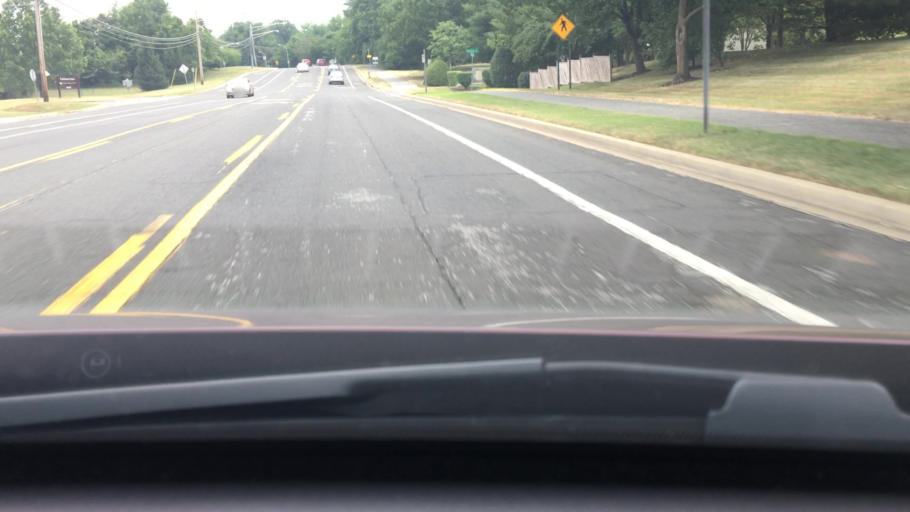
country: US
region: Maryland
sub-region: Montgomery County
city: Burtonsville
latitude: 39.0888
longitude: -76.9306
